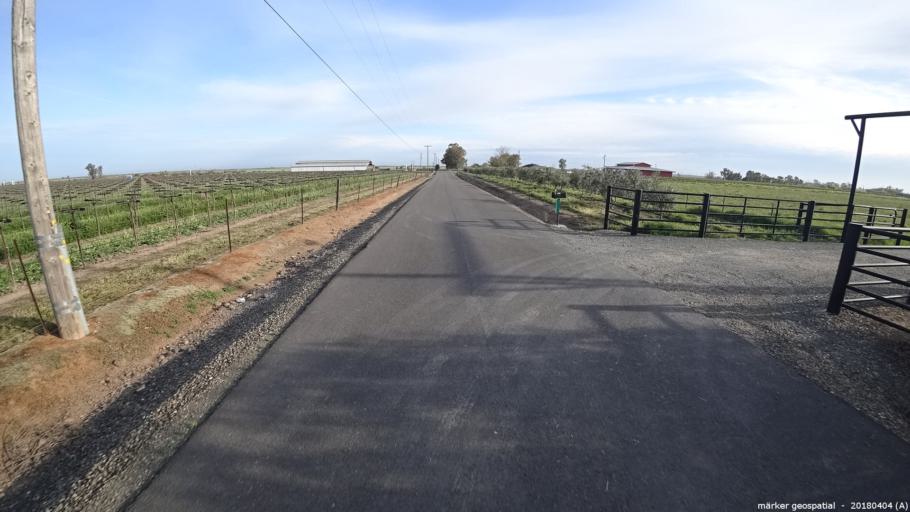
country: US
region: California
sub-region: Sacramento County
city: Herald
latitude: 38.3311
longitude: -121.2676
